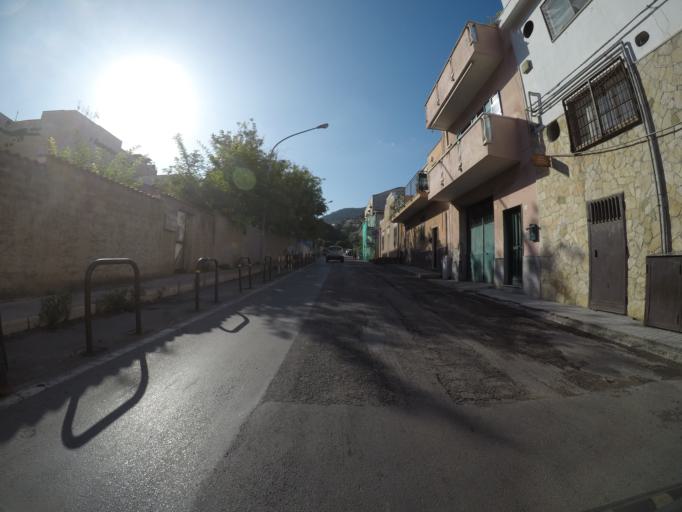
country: IT
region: Sicily
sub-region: Palermo
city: Isola delle Femmine
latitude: 38.1977
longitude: 13.2747
